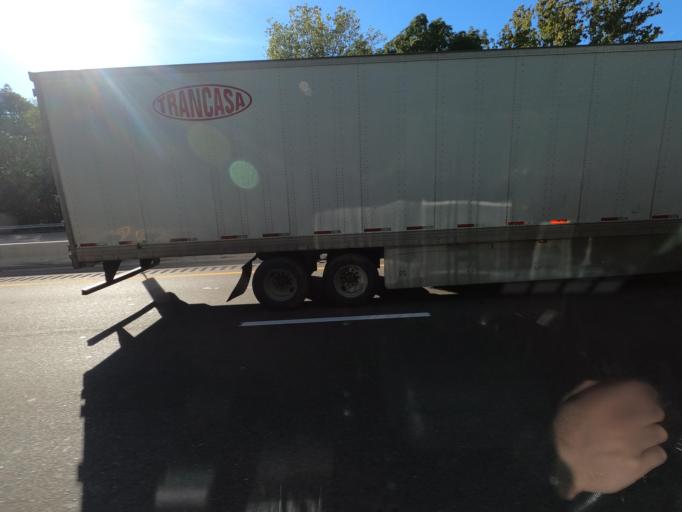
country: US
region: Tennessee
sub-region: Shelby County
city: Memphis
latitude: 35.1668
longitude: -90.0186
